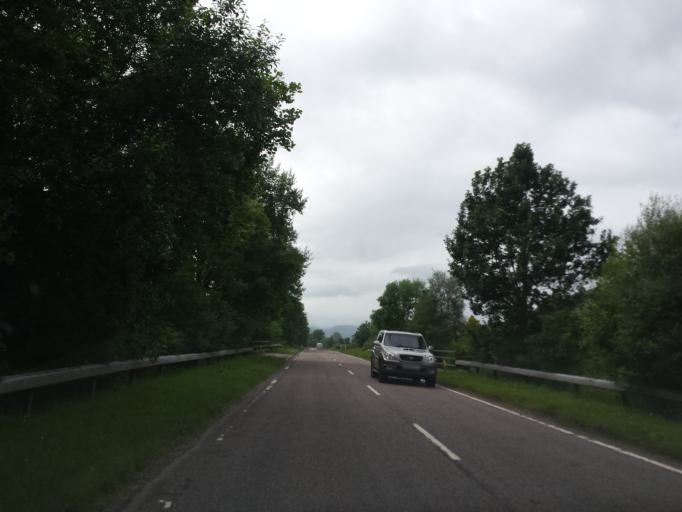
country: GB
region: Scotland
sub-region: Highland
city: Fort William
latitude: 56.8553
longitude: -5.2754
